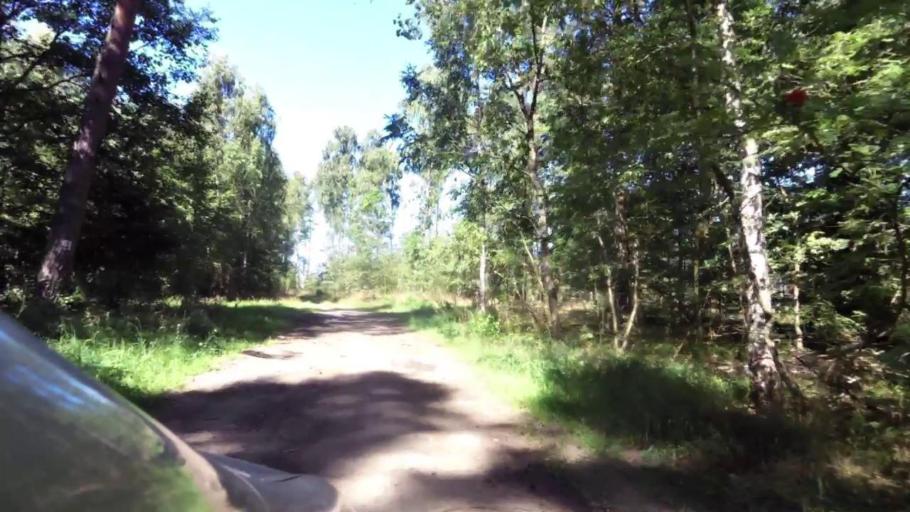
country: PL
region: West Pomeranian Voivodeship
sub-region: Powiat szczecinecki
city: Bialy Bor
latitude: 53.8318
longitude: 16.8704
